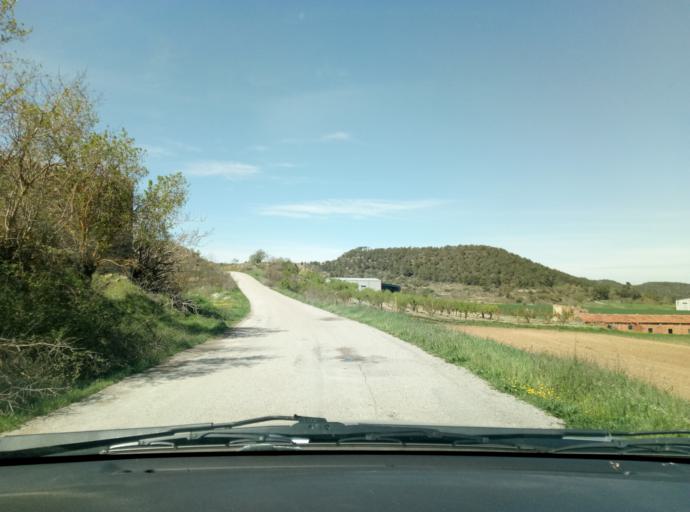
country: ES
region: Catalonia
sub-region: Provincia de Lleida
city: Fulleda
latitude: 41.4937
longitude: 0.9984
